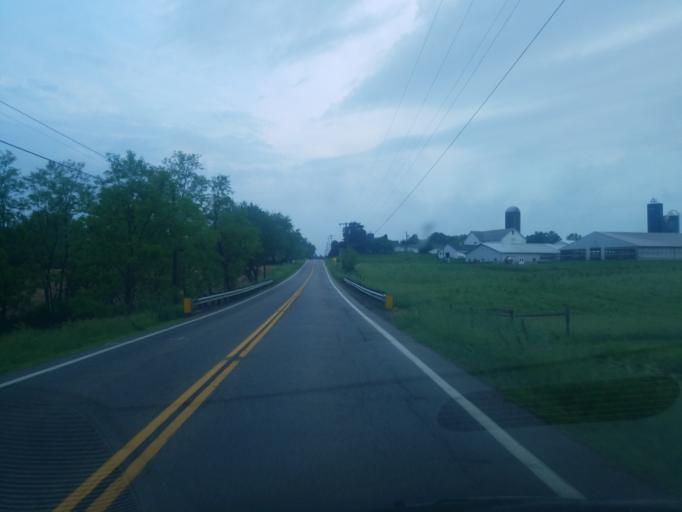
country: US
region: Ohio
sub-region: Columbiana County
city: Salem
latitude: 40.8597
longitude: -80.8886
